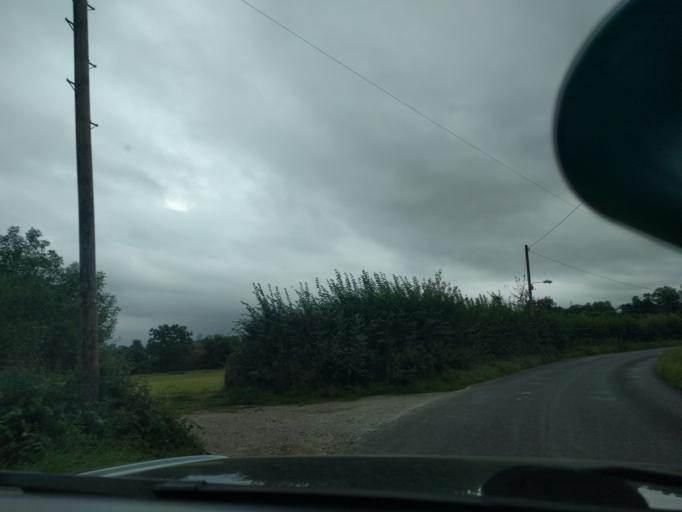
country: GB
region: England
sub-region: Wiltshire
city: Corsham
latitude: 51.4218
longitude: -2.1860
